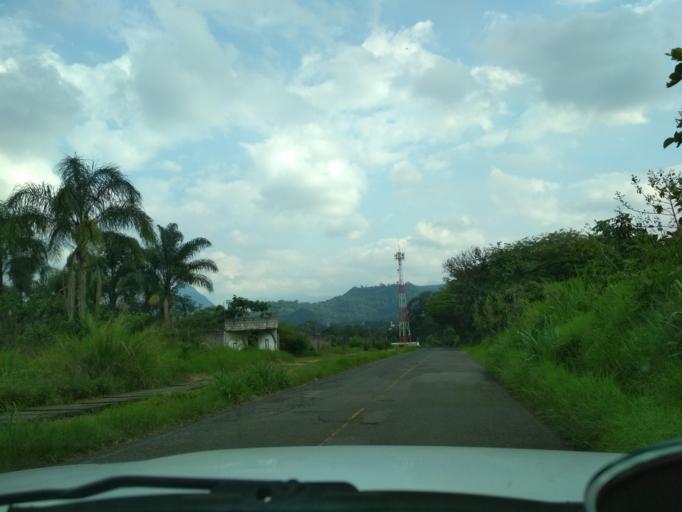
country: MX
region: Veracruz
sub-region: Fortin
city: Monte Salas
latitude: 18.9178
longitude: -97.0257
